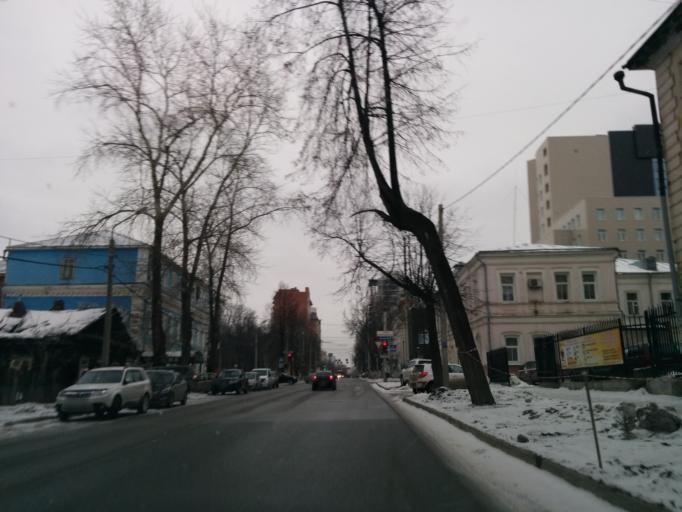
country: RU
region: Perm
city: Perm
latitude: 58.0147
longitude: 56.2571
